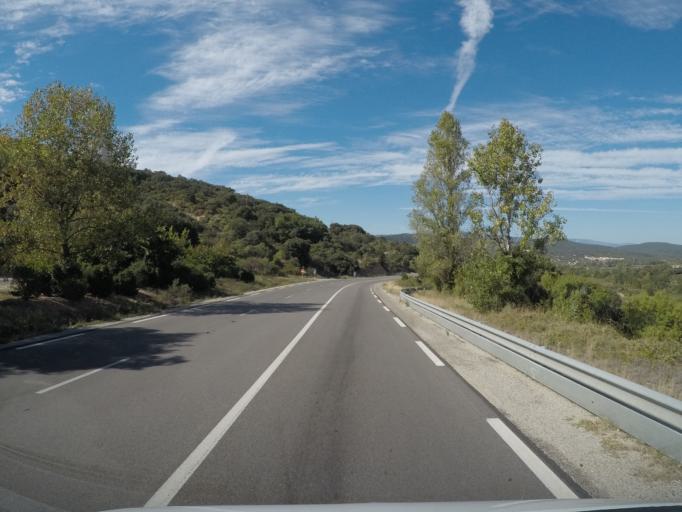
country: FR
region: Languedoc-Roussillon
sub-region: Departement de l'Herault
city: Saint-Martin-de-Londres
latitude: 43.7745
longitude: 3.7437
